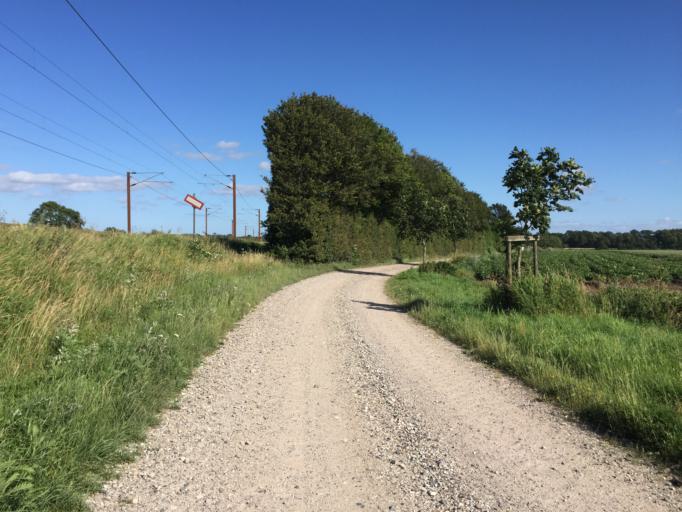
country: DK
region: South Denmark
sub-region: Kerteminde Kommune
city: Langeskov
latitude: 55.3733
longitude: 10.5419
